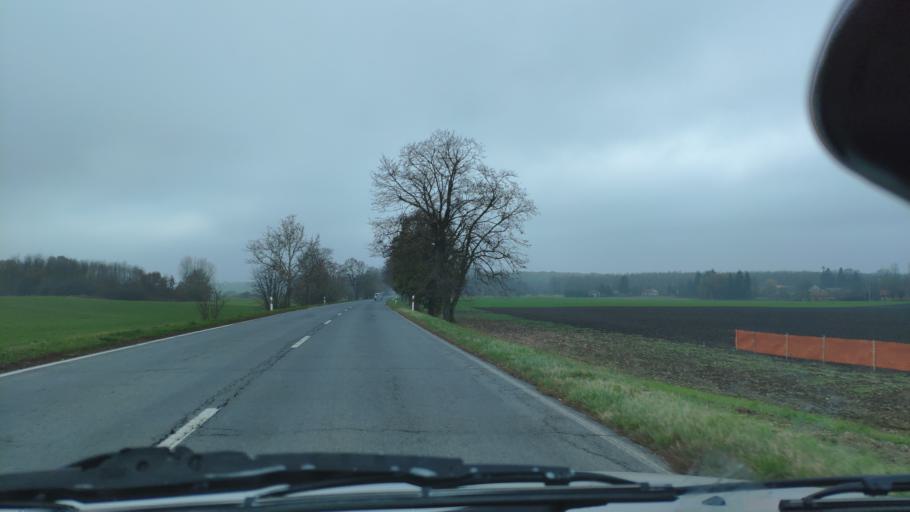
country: HU
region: Zala
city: Zalakomar
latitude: 46.5551
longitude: 17.2579
